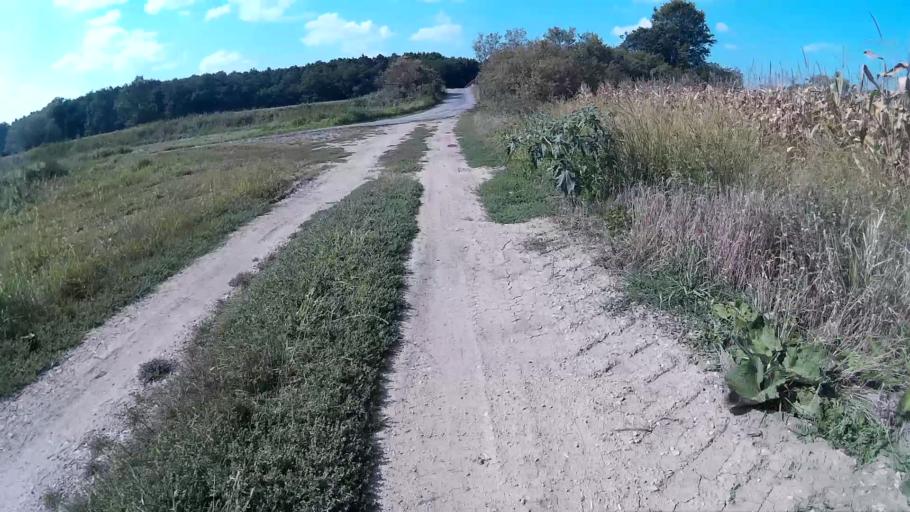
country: CZ
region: South Moravian
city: Hrusovany nad Jevisovkou
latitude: 48.7875
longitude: 16.4365
